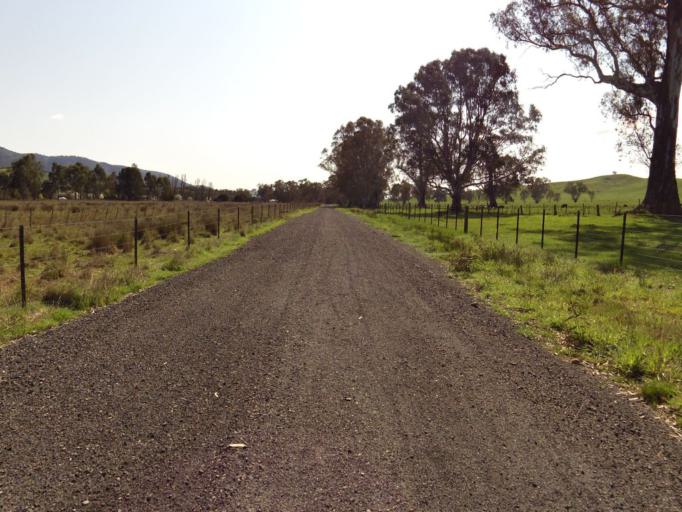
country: AU
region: Victoria
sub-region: Murrindindi
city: Alexandra
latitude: -37.1468
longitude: 145.5879
